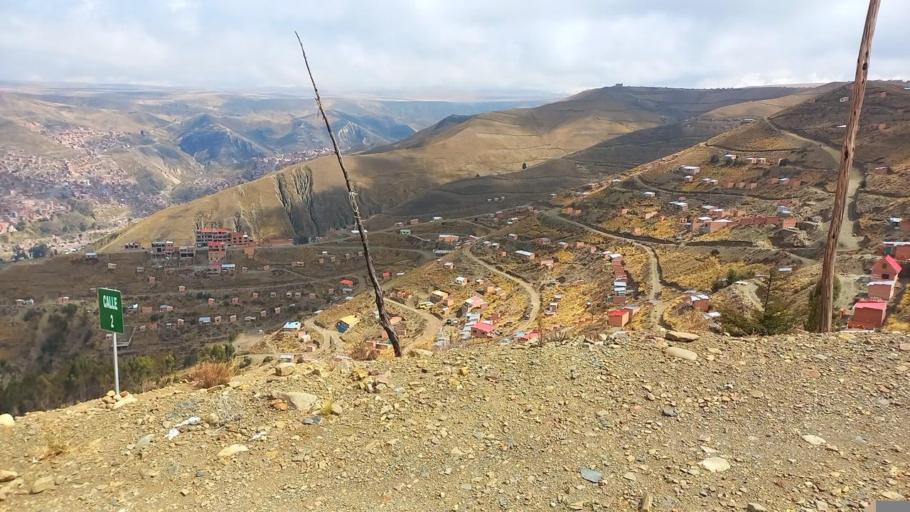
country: BO
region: La Paz
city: La Paz
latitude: -16.4653
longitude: -68.1398
